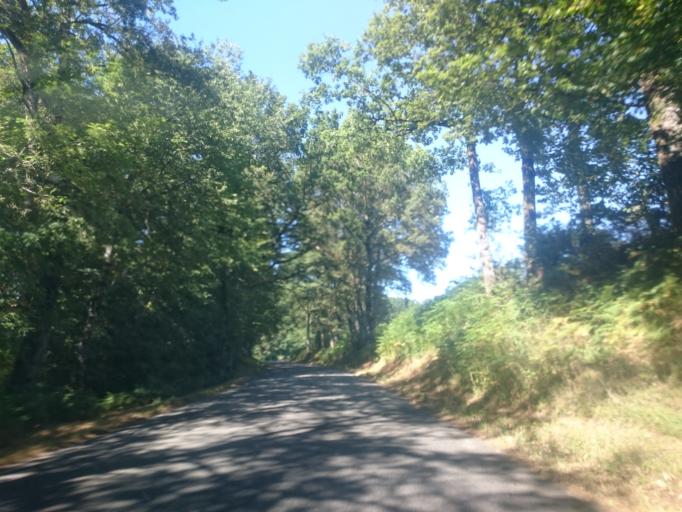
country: FR
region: Auvergne
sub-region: Departement du Cantal
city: Saint-Mamet-la-Salvetat
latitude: 44.8635
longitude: 2.2253
